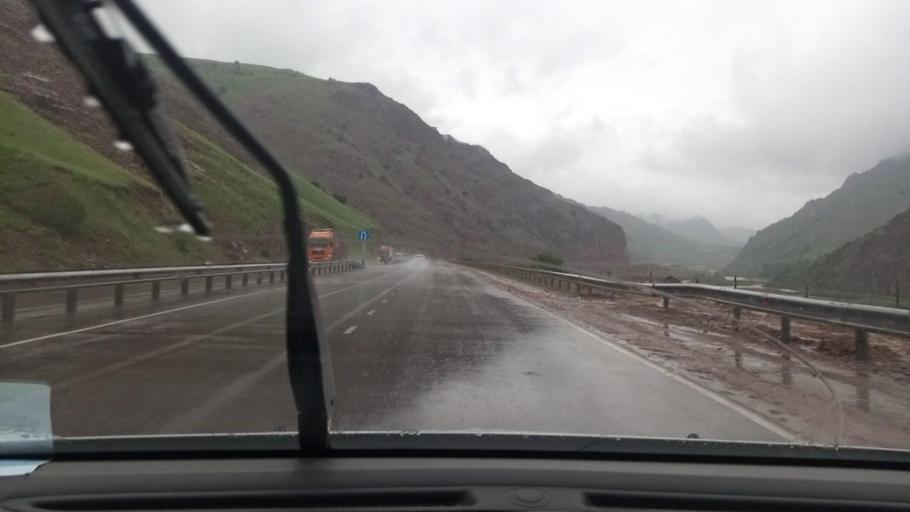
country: UZ
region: Toshkent
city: Angren
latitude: 41.1109
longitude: 70.3376
